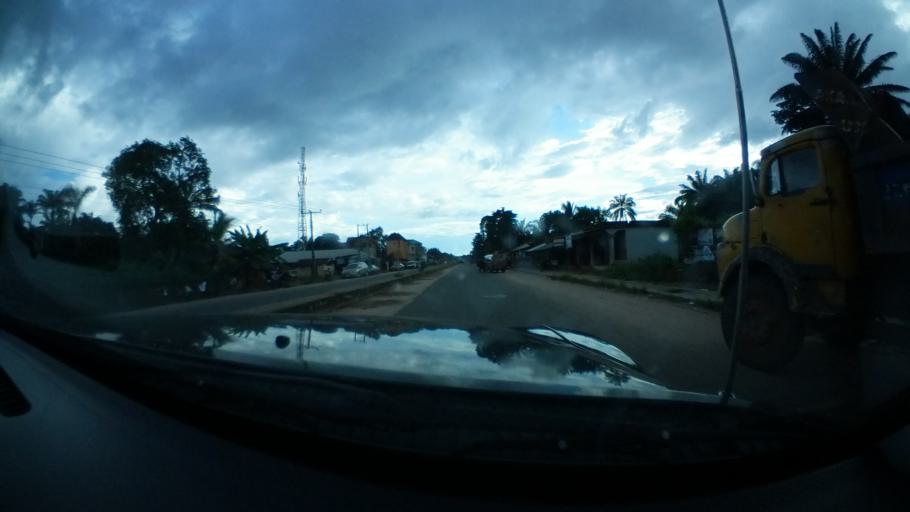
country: NG
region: Imo
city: Orlu
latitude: 5.7972
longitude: 7.0198
